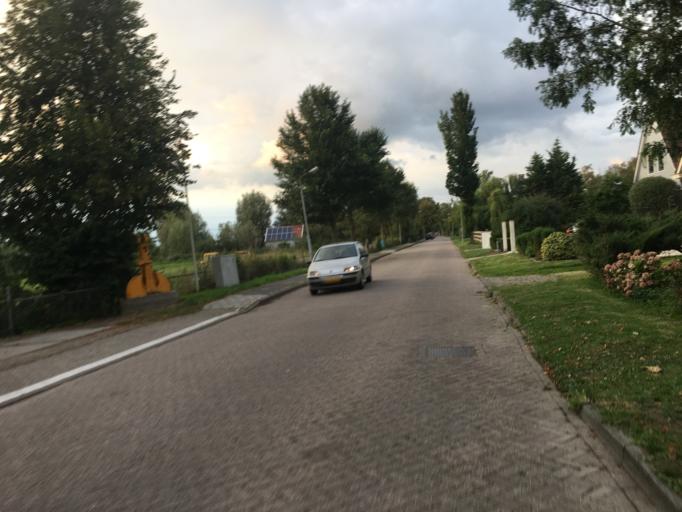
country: NL
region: North Holland
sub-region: Gemeente Zaanstad
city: Zaanstad
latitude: 52.4436
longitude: 4.7776
